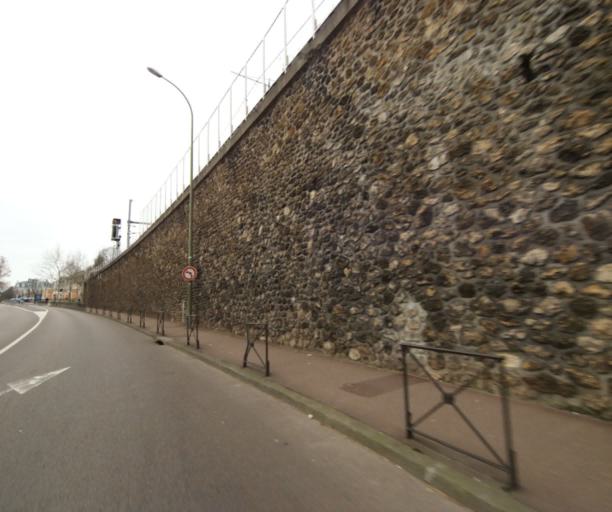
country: FR
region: Ile-de-France
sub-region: Departement des Hauts-de-Seine
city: Saint-Cloud
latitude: 48.8456
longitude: 2.2178
